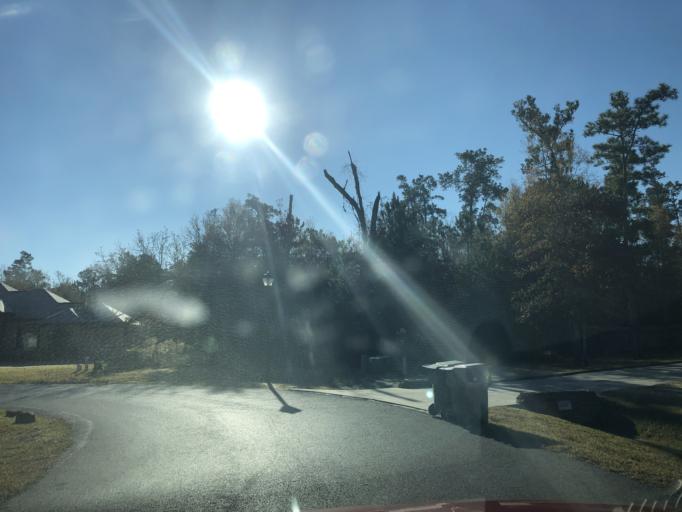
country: US
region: Texas
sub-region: Montgomery County
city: Porter Heights
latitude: 30.0680
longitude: -95.3217
